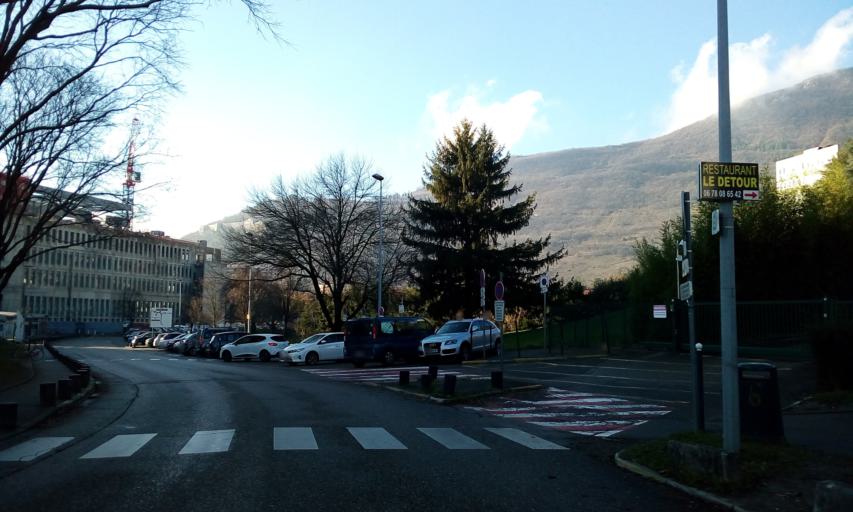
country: FR
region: Rhone-Alpes
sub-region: Departement de l'Isere
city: La Tronche
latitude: 45.2007
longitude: 5.7464
